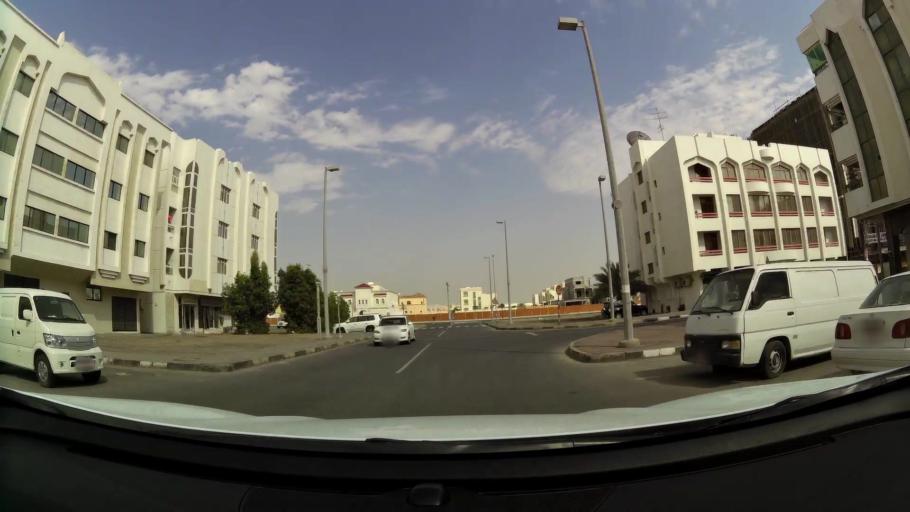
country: AE
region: Abu Dhabi
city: Abu Dhabi
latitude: 24.3359
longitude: 54.5375
